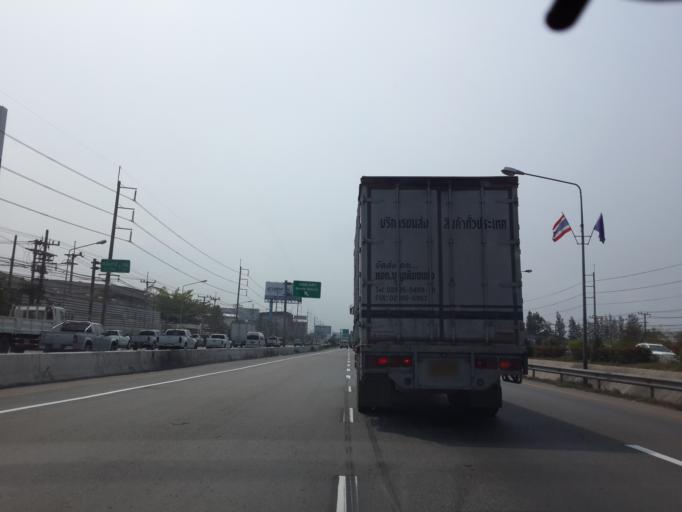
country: TH
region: Chon Buri
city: Chon Buri
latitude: 13.4477
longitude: 100.9991
